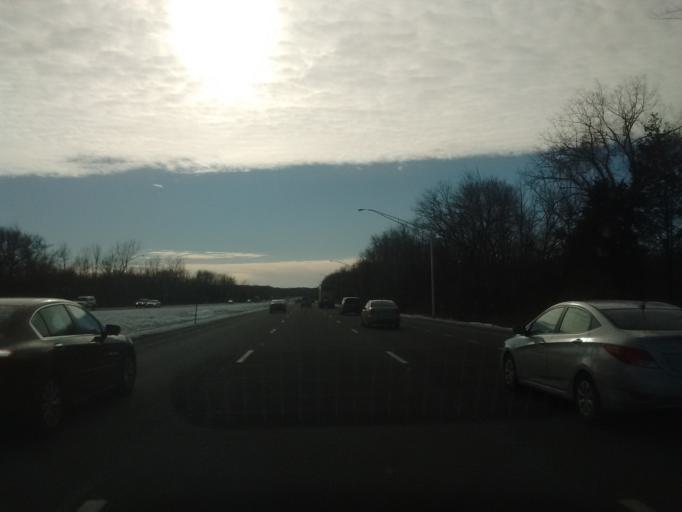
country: US
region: Connecticut
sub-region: Hartford County
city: Farmington
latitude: 41.7173
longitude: -72.7970
